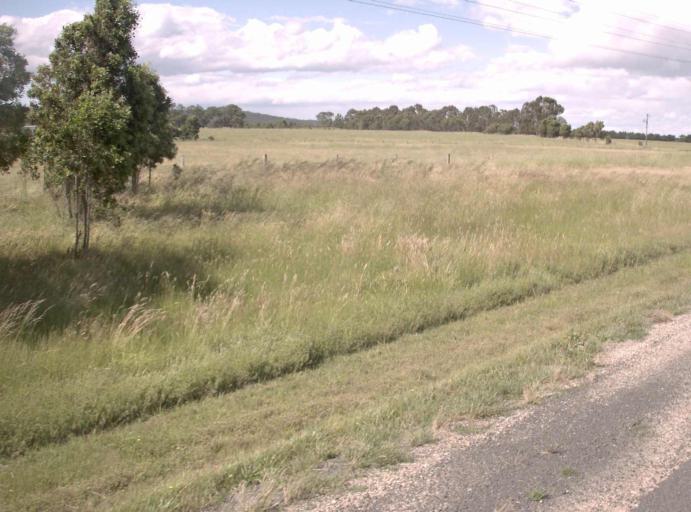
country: AU
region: Victoria
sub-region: Latrobe
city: Traralgon
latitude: -38.1384
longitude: 146.5363
